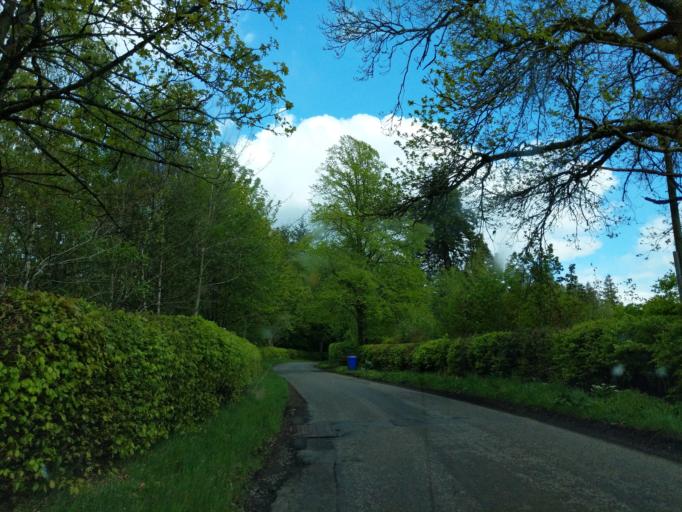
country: GB
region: Scotland
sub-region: Stirling
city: Callander
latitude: 56.1638
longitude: -4.2631
